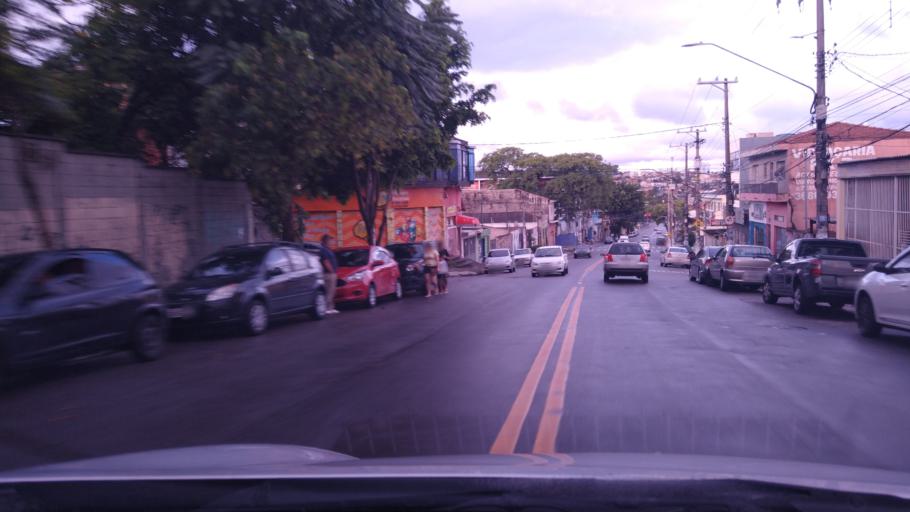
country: BR
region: Sao Paulo
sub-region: Osasco
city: Osasco
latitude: -23.5143
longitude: -46.7783
